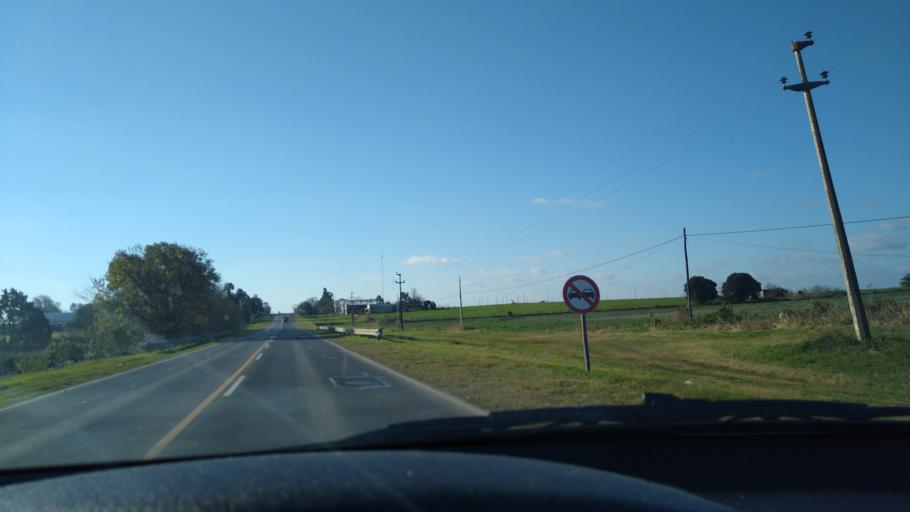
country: AR
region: Entre Rios
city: Oro Verde
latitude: -31.9377
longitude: -60.5864
